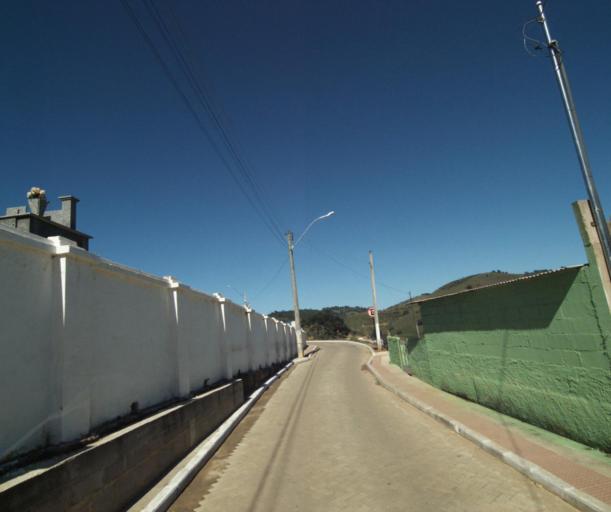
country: BR
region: Minas Gerais
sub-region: Espera Feliz
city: Espera Feliz
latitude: -20.6919
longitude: -41.8474
